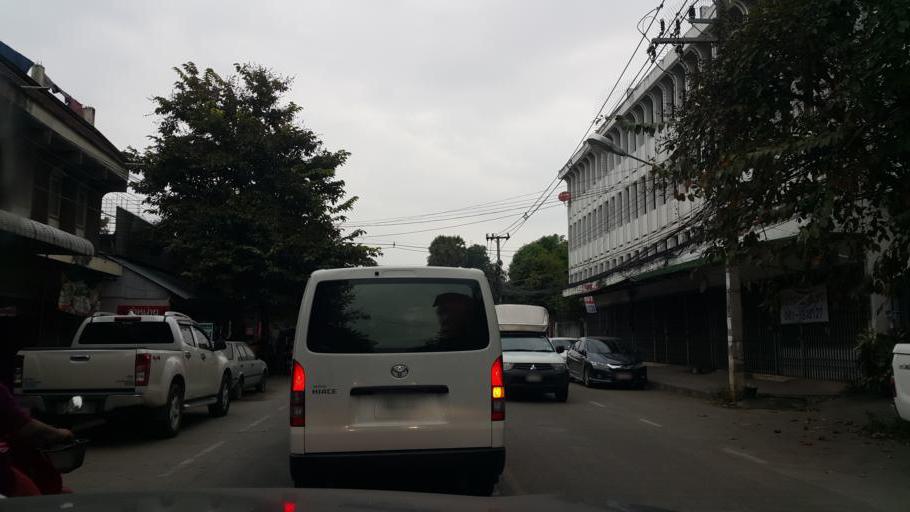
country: TH
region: Chiang Mai
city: Chiang Mai
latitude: 18.8003
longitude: 98.9985
